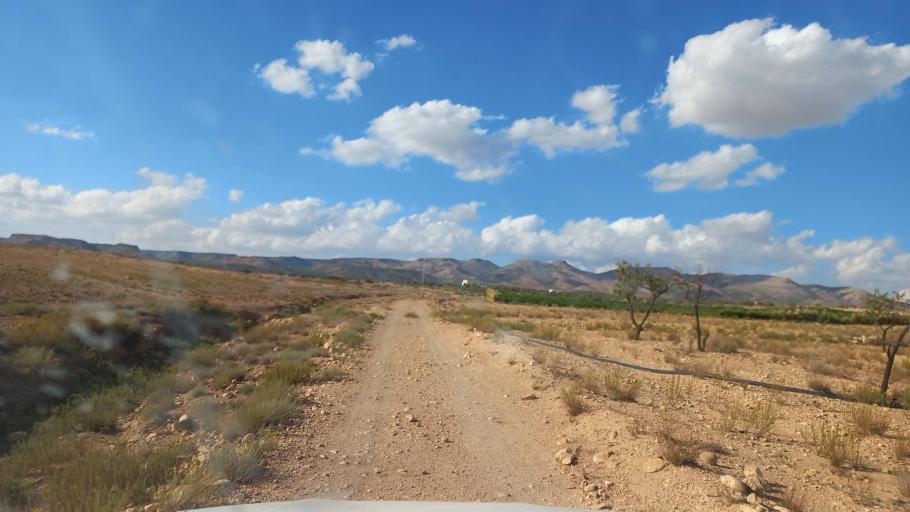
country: TN
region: Al Qasrayn
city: Sbiba
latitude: 35.3986
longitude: 9.0315
